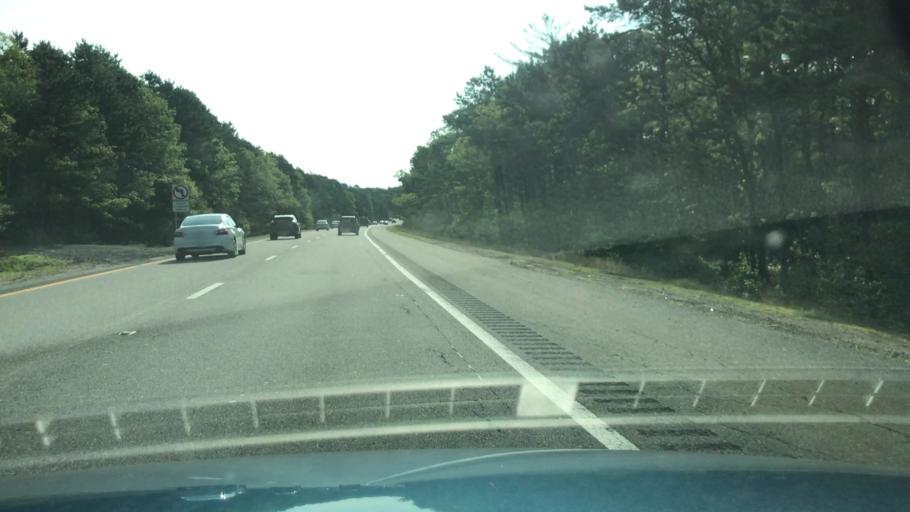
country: US
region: Massachusetts
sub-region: Barnstable County
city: Barnstable
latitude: 41.6890
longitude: -70.3291
